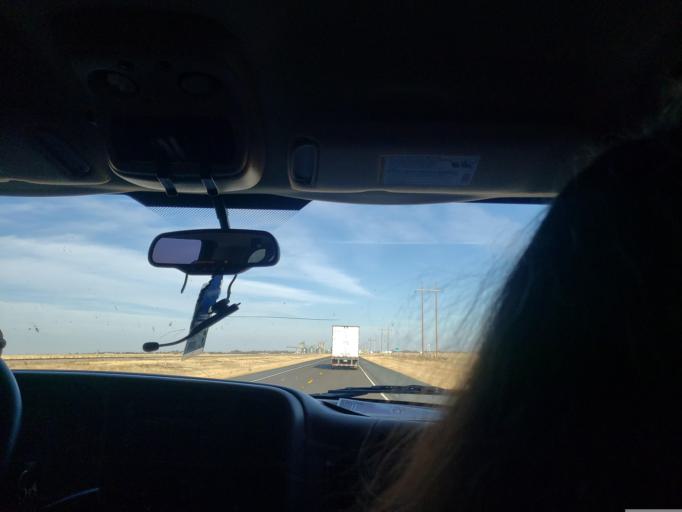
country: US
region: Oklahoma
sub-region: Texas County
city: Goodwell
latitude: 36.4864
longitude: -101.8104
